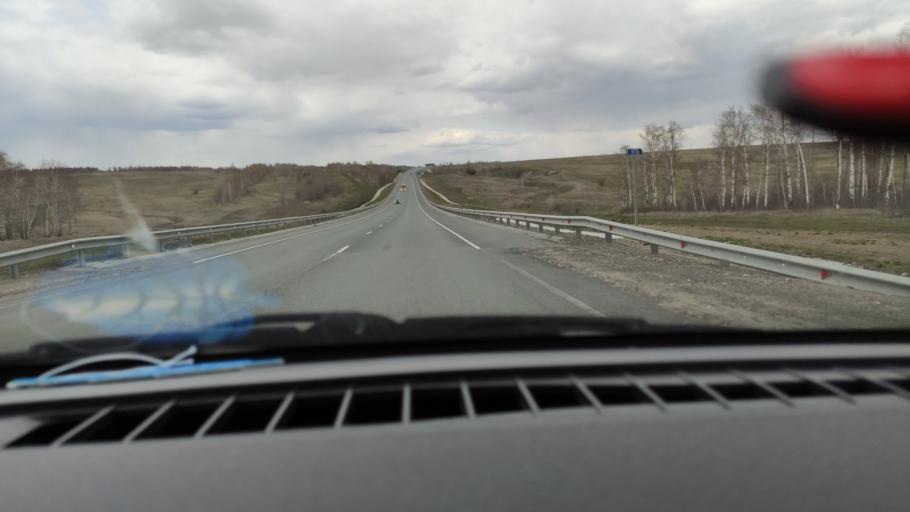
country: RU
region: Saratov
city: Shikhany
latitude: 52.1271
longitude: 47.2390
